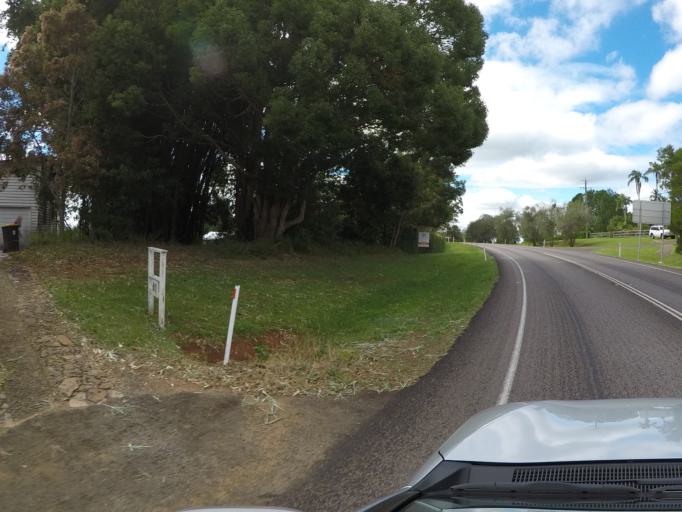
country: AU
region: Queensland
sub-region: Sunshine Coast
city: Nambour
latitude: -26.6324
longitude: 152.8681
